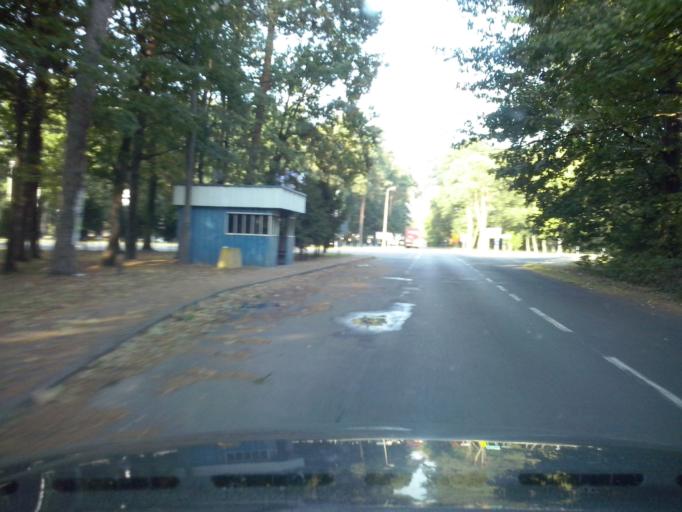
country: PL
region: Subcarpathian Voivodeship
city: Nowa Sarzyna
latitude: 50.3263
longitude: 22.3350
